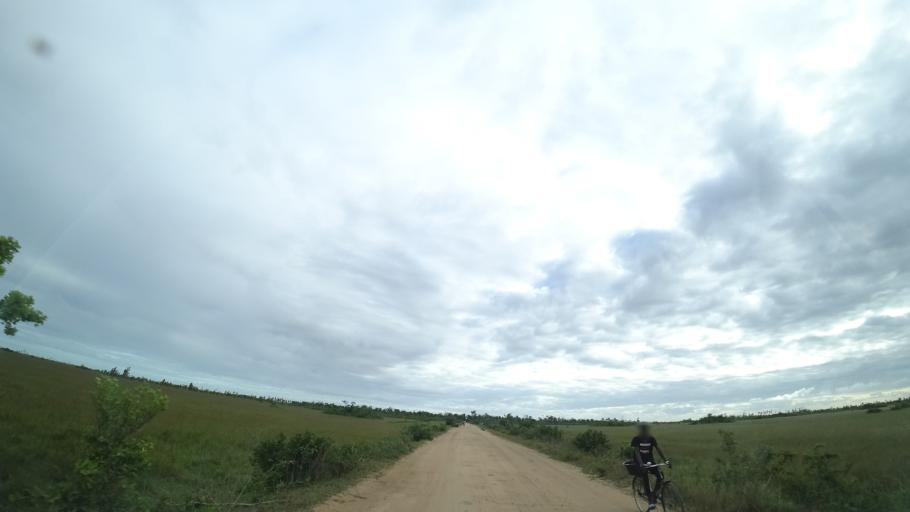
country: MZ
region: Sofala
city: Beira
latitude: -19.7343
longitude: 34.9746
